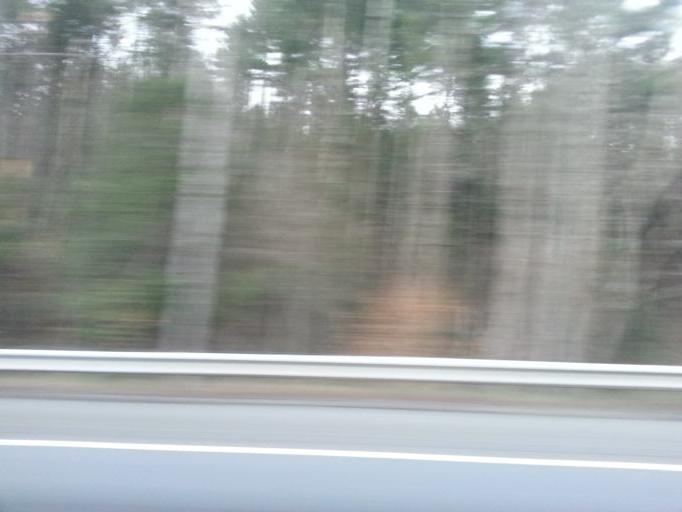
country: US
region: North Carolina
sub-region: Haywood County
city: Cove Creek
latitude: 35.6773
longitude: -83.0264
